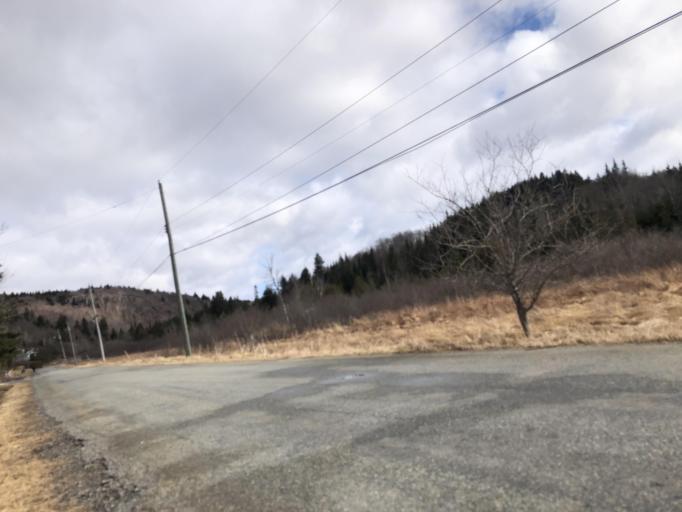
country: CA
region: New Brunswick
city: Saint John
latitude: 45.3259
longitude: -66.0125
